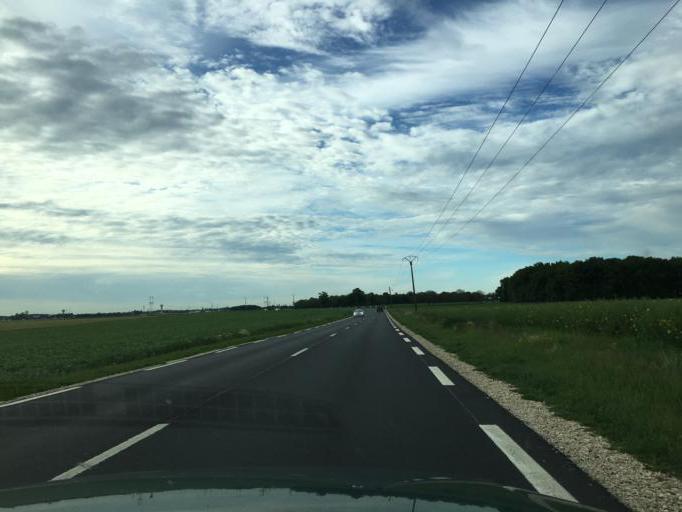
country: FR
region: Centre
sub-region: Departement du Loiret
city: Ormes
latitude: 47.9605
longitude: 1.7892
